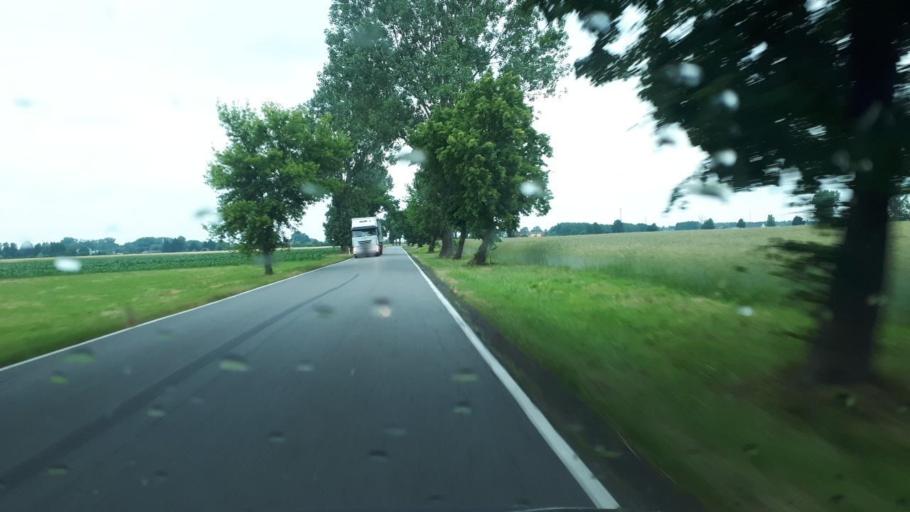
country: PL
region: Greater Poland Voivodeship
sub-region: Powiat ostrowski
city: Odolanow
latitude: 51.5593
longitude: 17.6977
